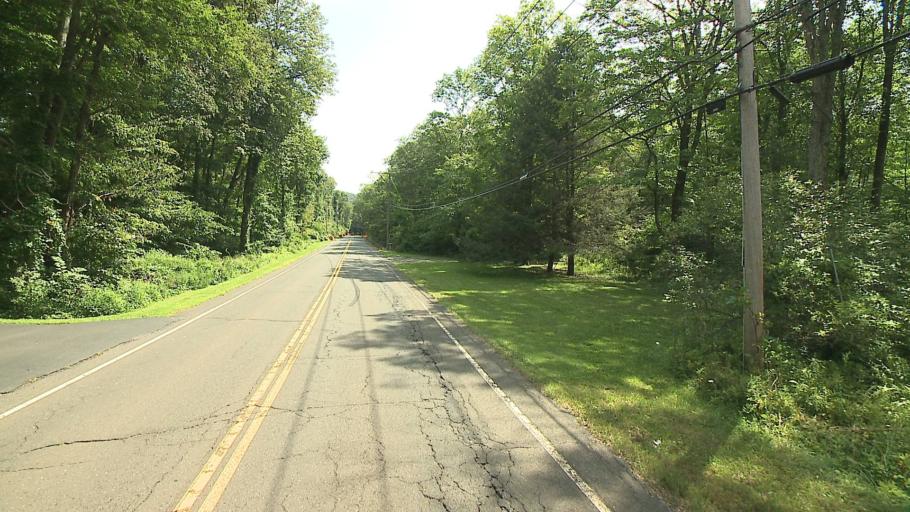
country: US
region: New York
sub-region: Putnam County
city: Putnam Lake
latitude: 41.4709
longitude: -73.5087
